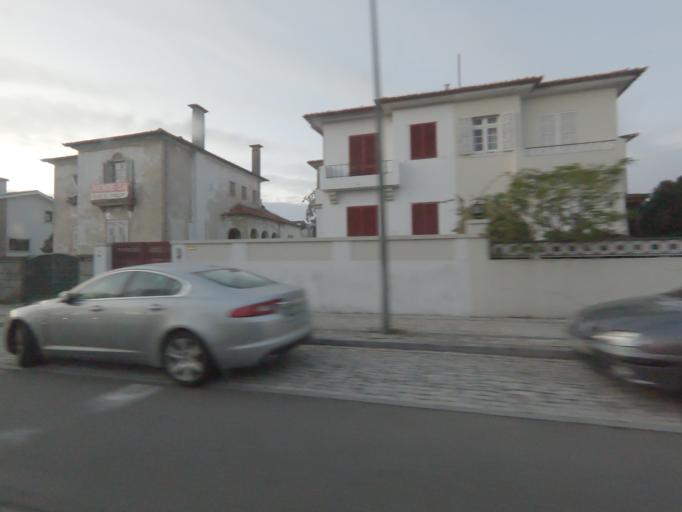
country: PT
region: Porto
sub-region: Matosinhos
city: Senhora da Hora
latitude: 41.1595
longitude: -8.6619
